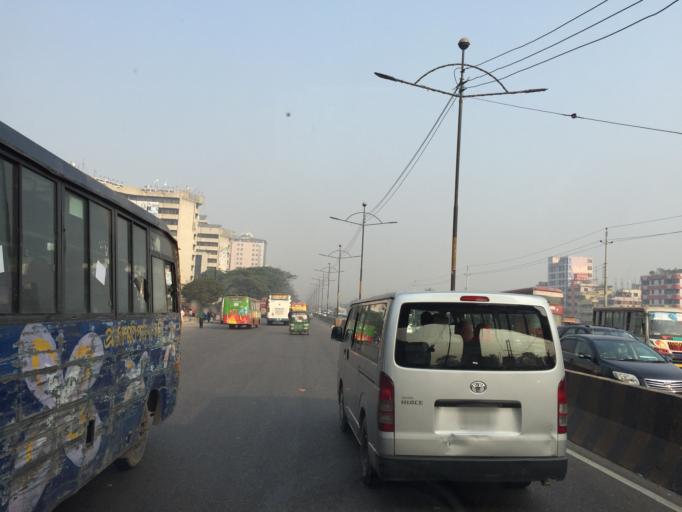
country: BD
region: Dhaka
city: Tungi
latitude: 23.8292
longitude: 90.4199
